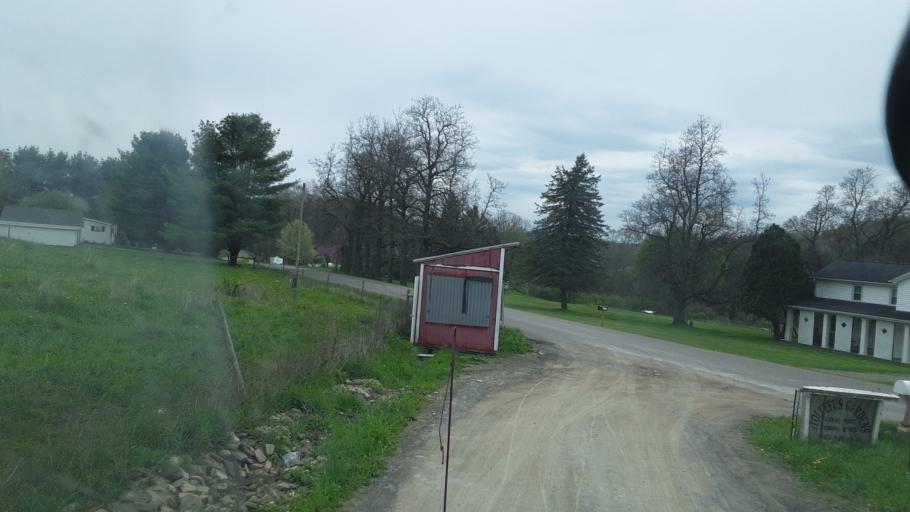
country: US
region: New York
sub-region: Steuben County
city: Addison
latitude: 42.0984
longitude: -77.2619
